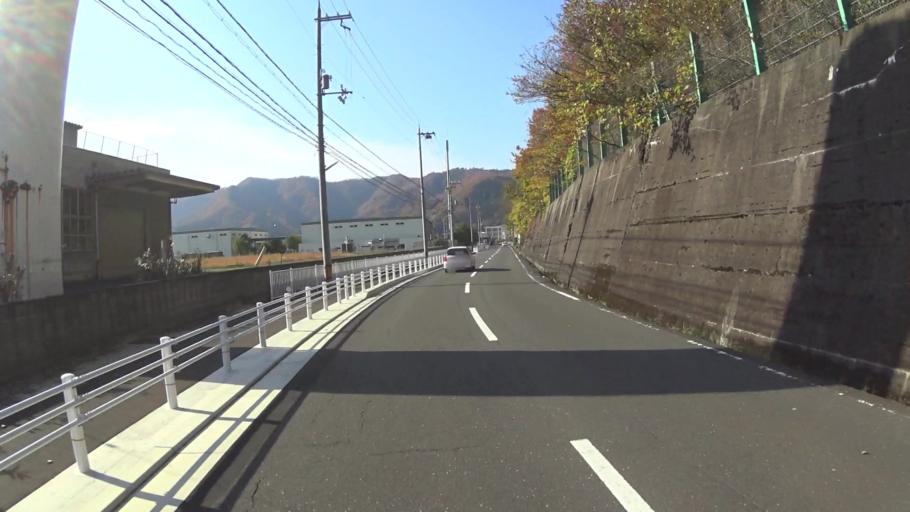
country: JP
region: Kyoto
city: Maizuru
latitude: 35.5166
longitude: 135.4005
